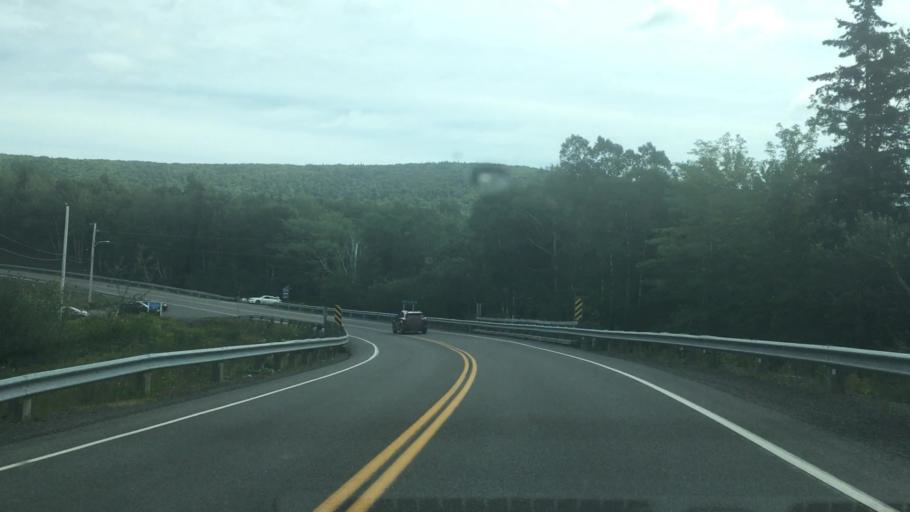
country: CA
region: Nova Scotia
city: Sydney Mines
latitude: 46.3079
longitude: -60.6196
